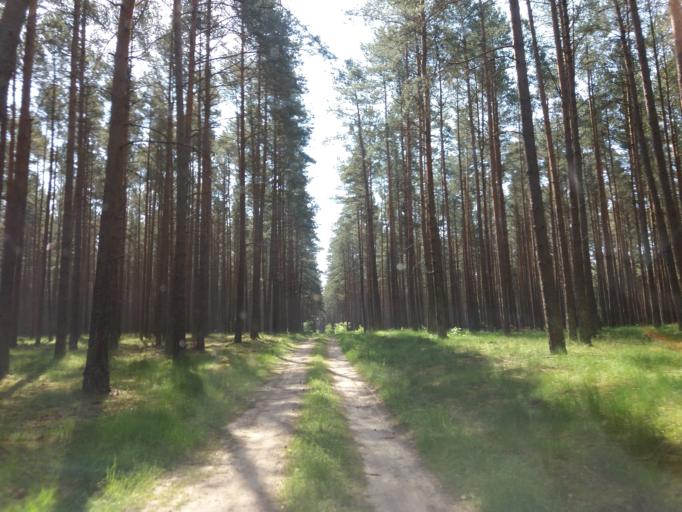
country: PL
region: West Pomeranian Voivodeship
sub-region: Powiat choszczenski
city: Bierzwnik
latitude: 53.1130
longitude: 15.6911
